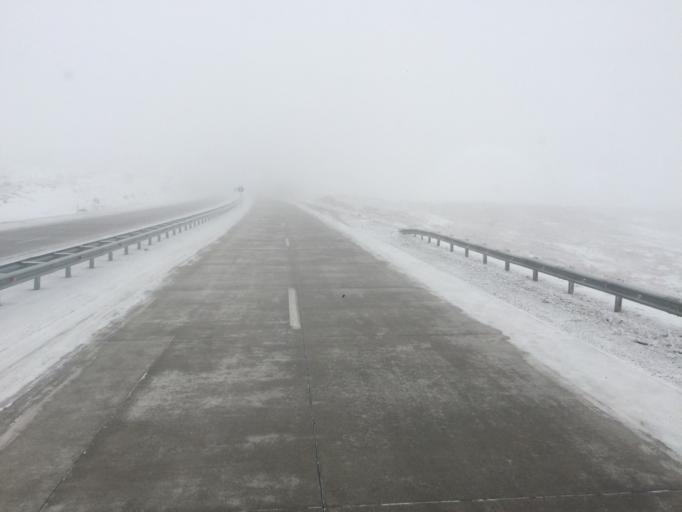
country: KZ
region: Zhambyl
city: Georgiyevka
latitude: 43.4210
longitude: 74.9697
